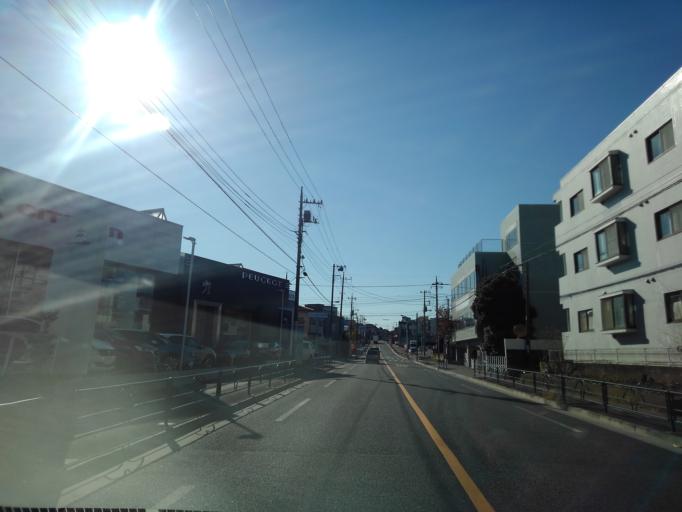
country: JP
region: Tokyo
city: Hino
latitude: 35.6885
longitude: 139.3706
